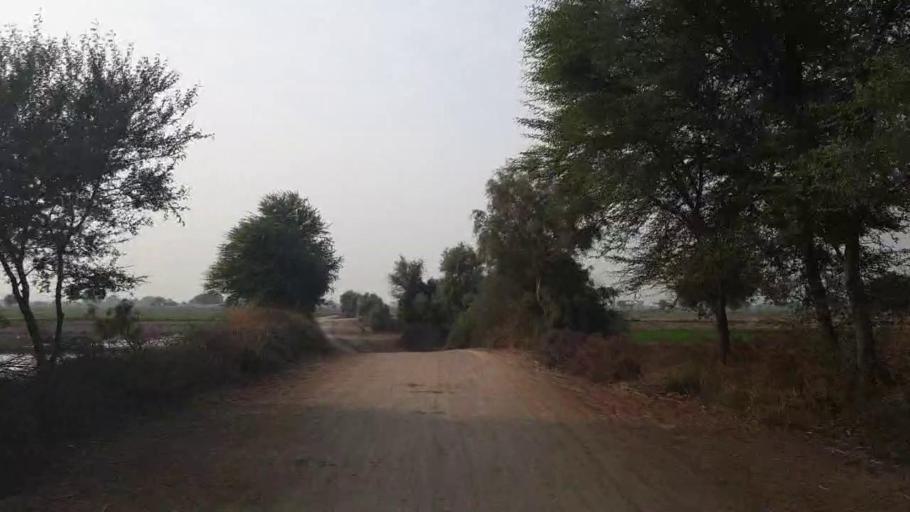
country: PK
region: Sindh
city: Sann
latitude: 26.1426
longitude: 68.0477
